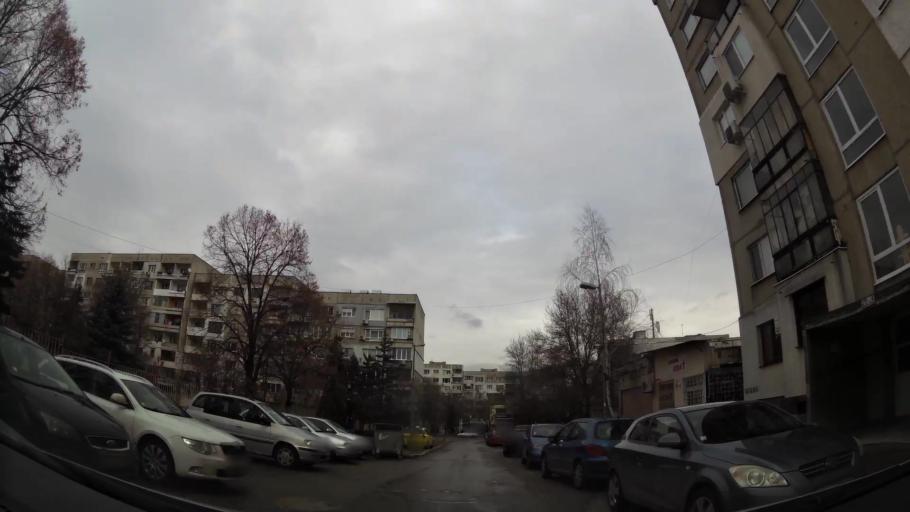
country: BG
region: Sofiya
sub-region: Obshtina Bozhurishte
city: Bozhurishte
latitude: 42.7250
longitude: 23.2540
